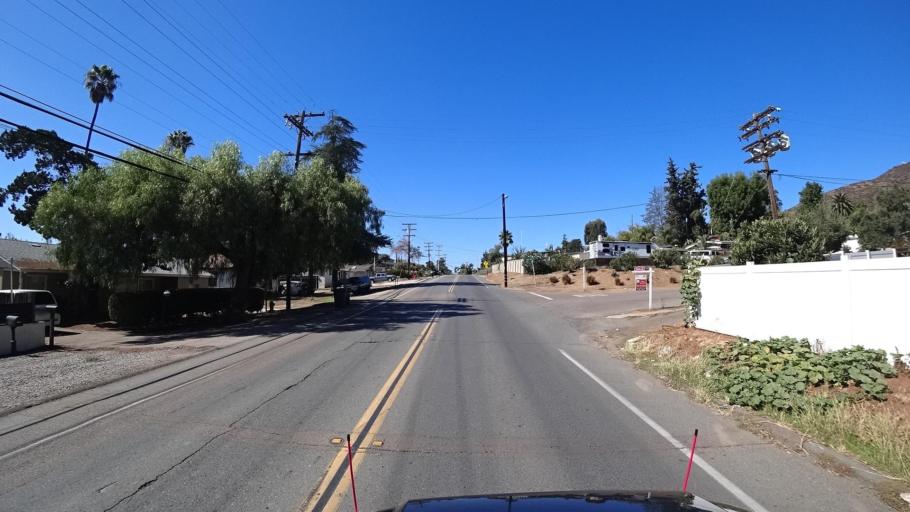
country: US
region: California
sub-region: San Diego County
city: Winter Gardens
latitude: 32.8208
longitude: -116.9363
